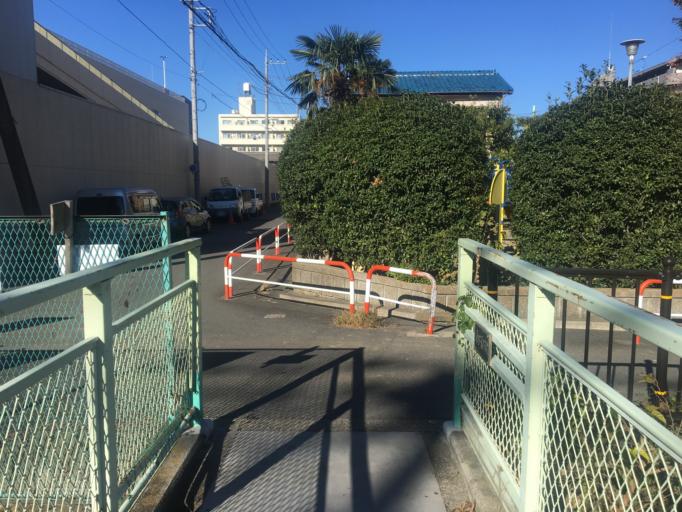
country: JP
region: Saitama
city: Shimotoda
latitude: 35.8062
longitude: 139.6721
